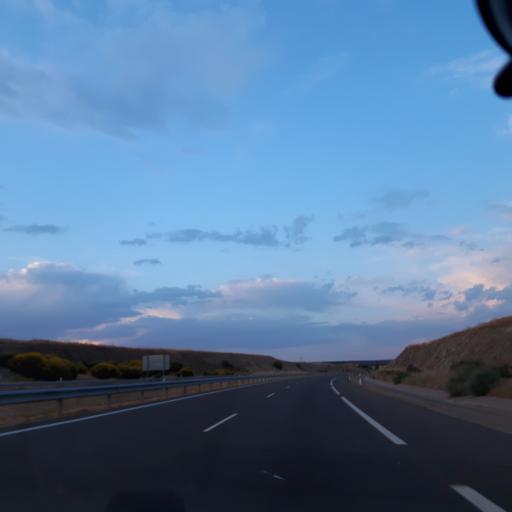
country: ES
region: Castille and Leon
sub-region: Provincia de Salamanca
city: Mozarbez
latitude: 40.8602
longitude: -5.6427
